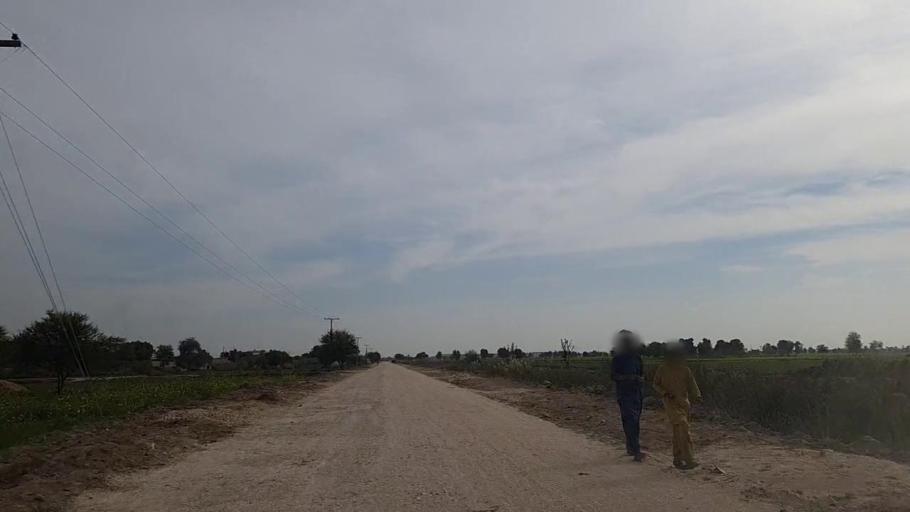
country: PK
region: Sindh
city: Daur
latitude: 26.4140
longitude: 68.4899
